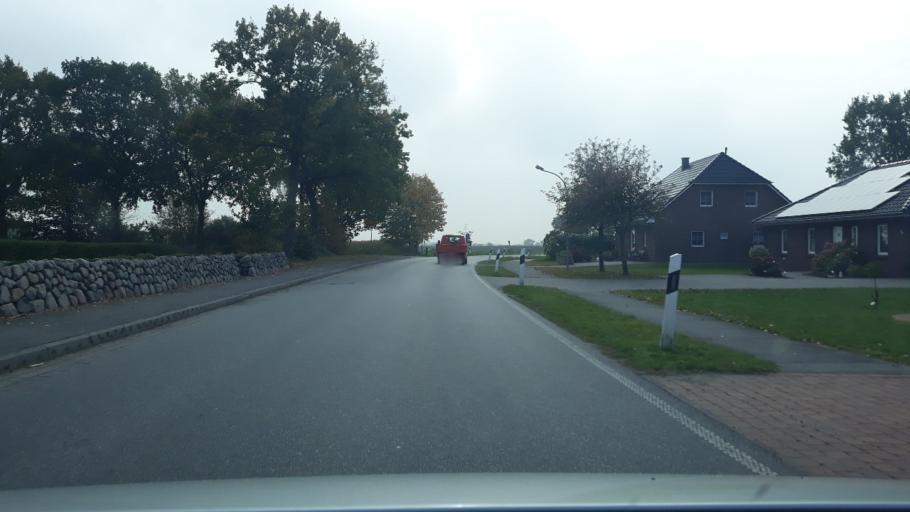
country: DE
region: Schleswig-Holstein
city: Klein Rheide
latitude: 54.4475
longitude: 9.4768
